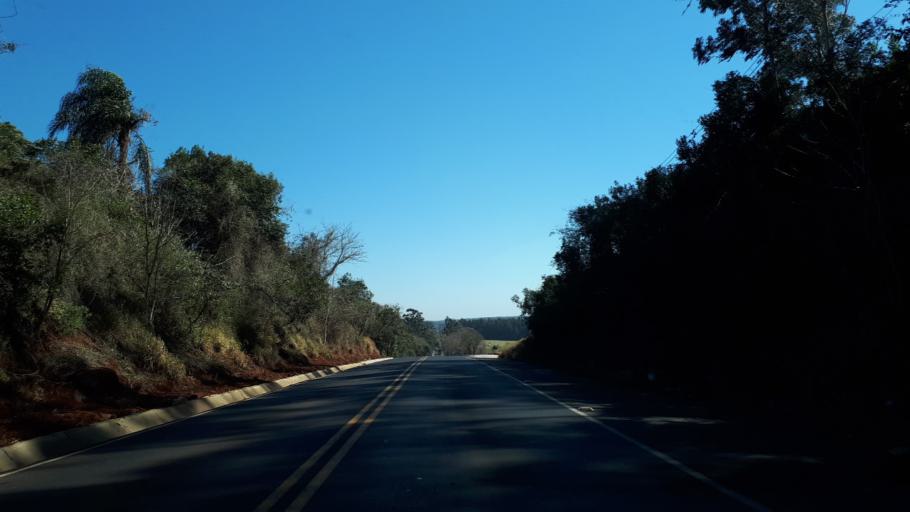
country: BR
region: Santa Catarina
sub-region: Chapeco
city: Chapeco
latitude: -27.0932
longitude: -52.7137
